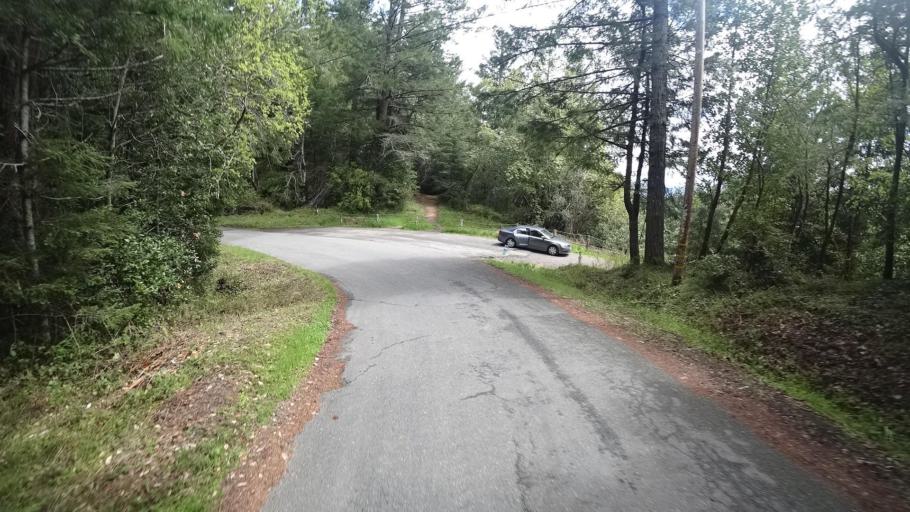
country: US
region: California
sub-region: Humboldt County
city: Blue Lake
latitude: 40.7996
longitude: -123.9839
